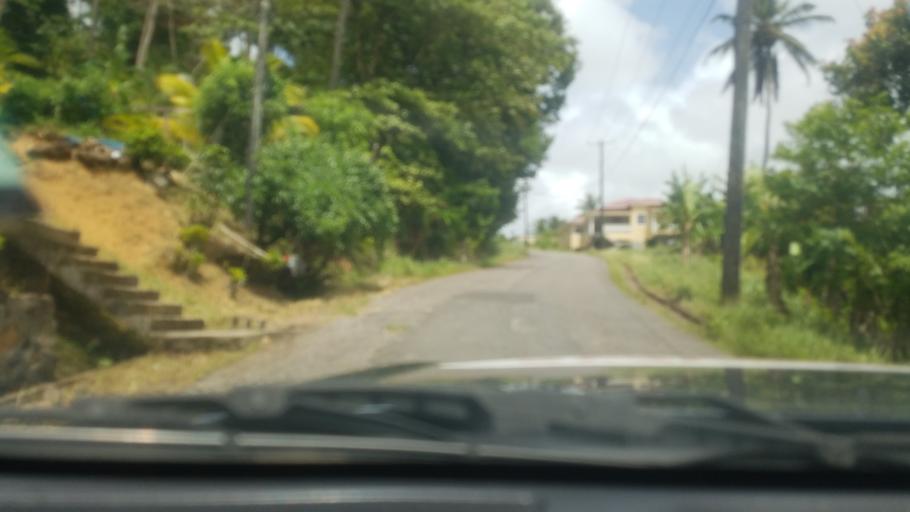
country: LC
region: Micoud Quarter
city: Micoud
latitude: 13.7976
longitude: -60.9481
